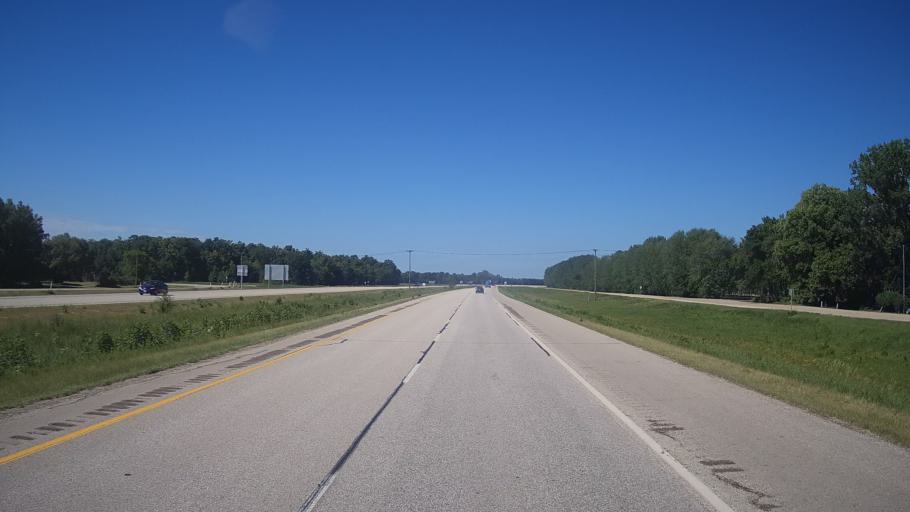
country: CA
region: Manitoba
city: Portage la Prairie
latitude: 49.9510
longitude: -98.2827
